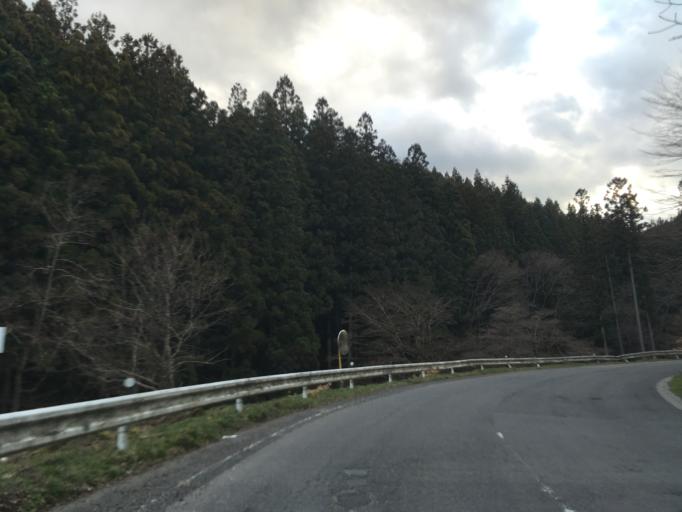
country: JP
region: Fukushima
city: Ishikawa
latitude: 37.0634
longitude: 140.5105
